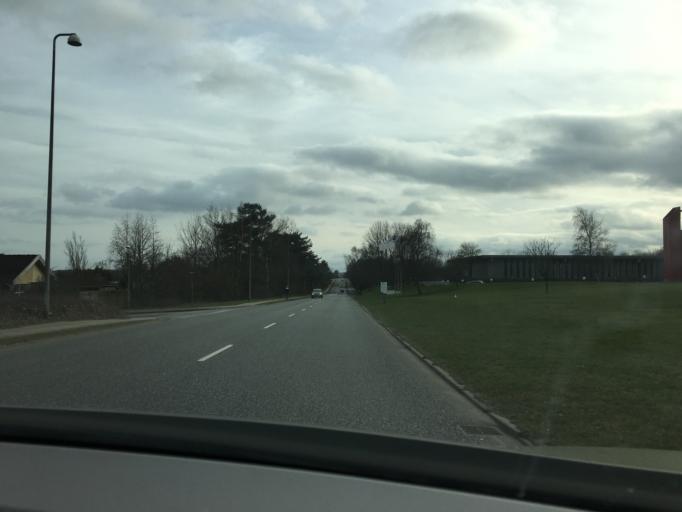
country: DK
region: South Denmark
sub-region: Vejle Kommune
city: Vejle
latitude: 55.7238
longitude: 9.5977
